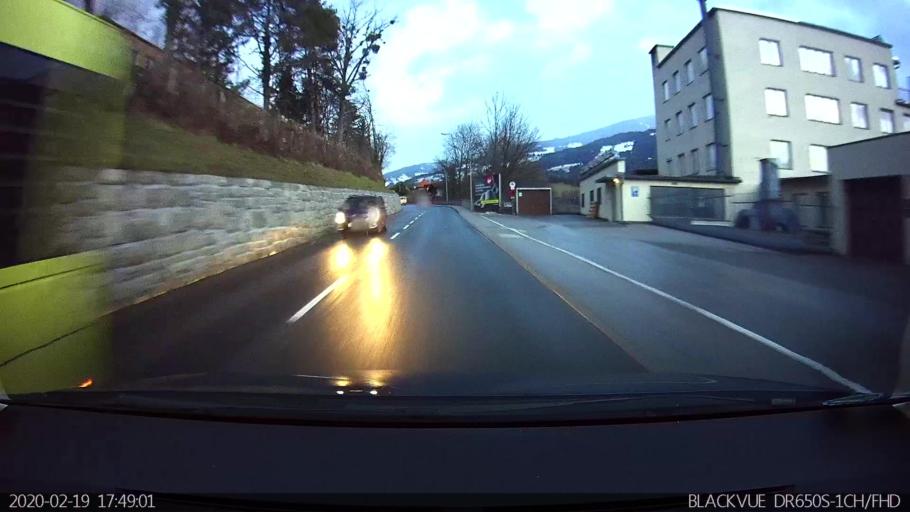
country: AT
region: Tyrol
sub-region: Politischer Bezirk Innsbruck Land
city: Hall in Tirol
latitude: 47.2805
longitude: 11.5170
